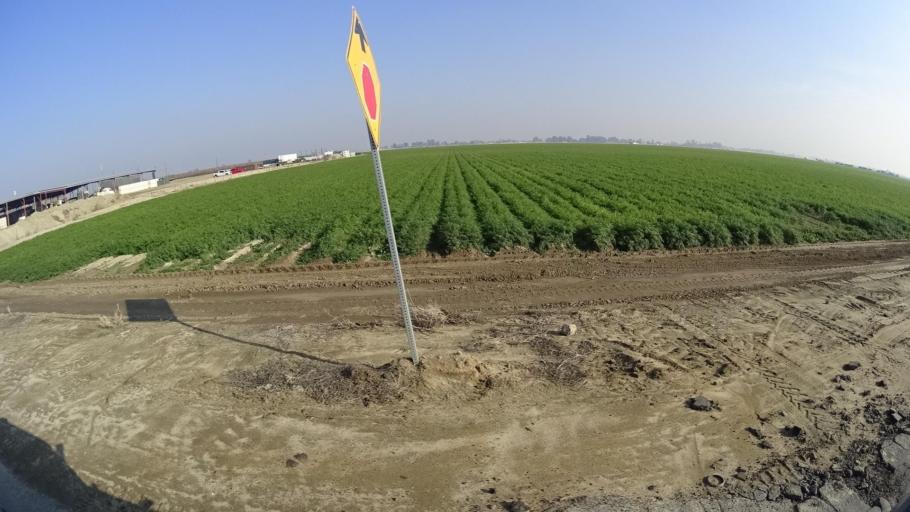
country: US
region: California
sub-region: Kern County
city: Greenfield
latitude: 35.2358
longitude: -119.0390
